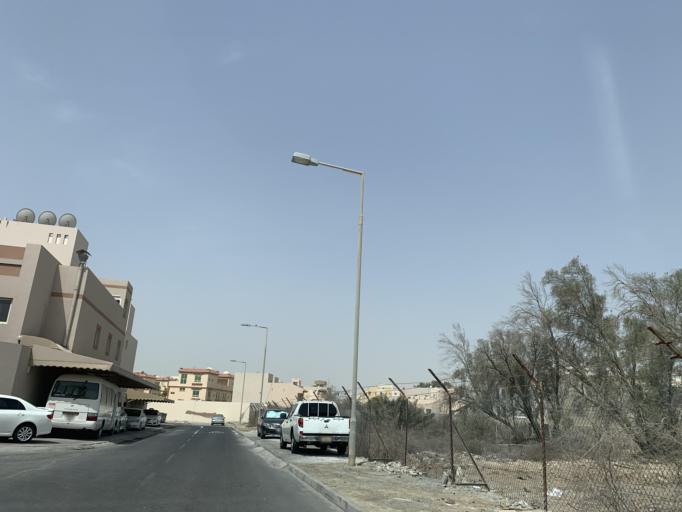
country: BH
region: Northern
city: Madinat `Isa
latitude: 26.1730
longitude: 50.5250
